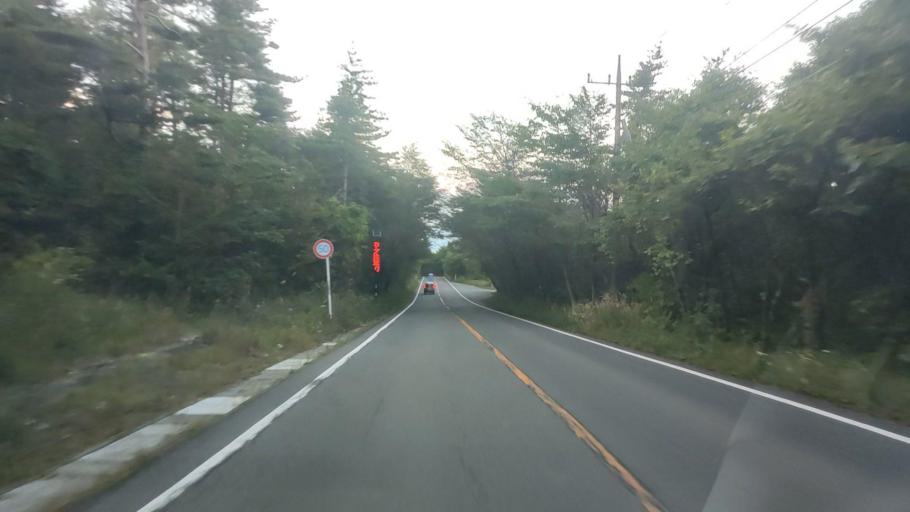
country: JP
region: Nagano
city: Komoro
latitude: 36.4237
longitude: 138.5713
